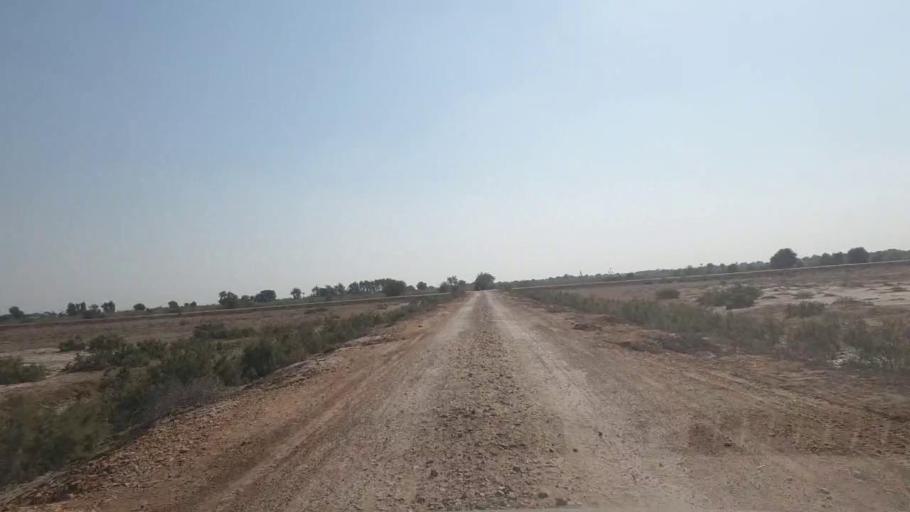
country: PK
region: Sindh
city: Chambar
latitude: 25.2962
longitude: 68.7418
